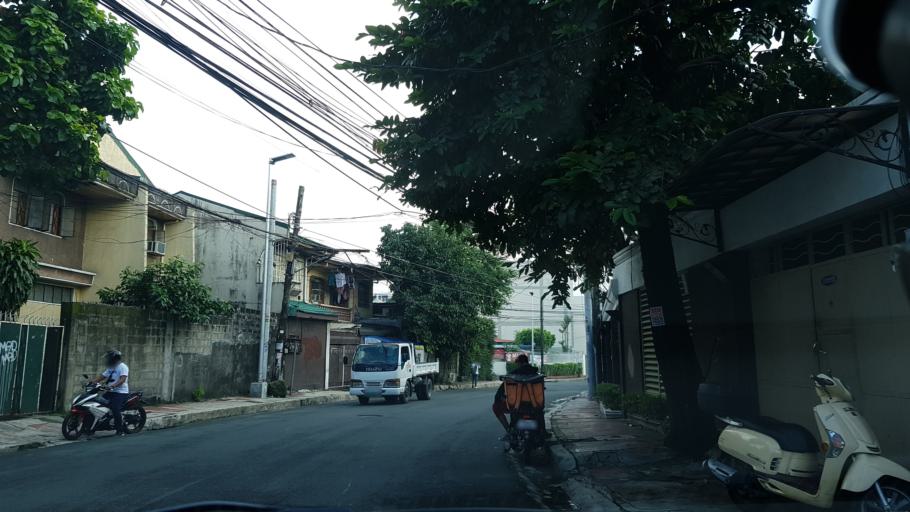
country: PH
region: Metro Manila
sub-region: Quezon City
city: Quezon City
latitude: 14.6391
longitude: 121.0580
